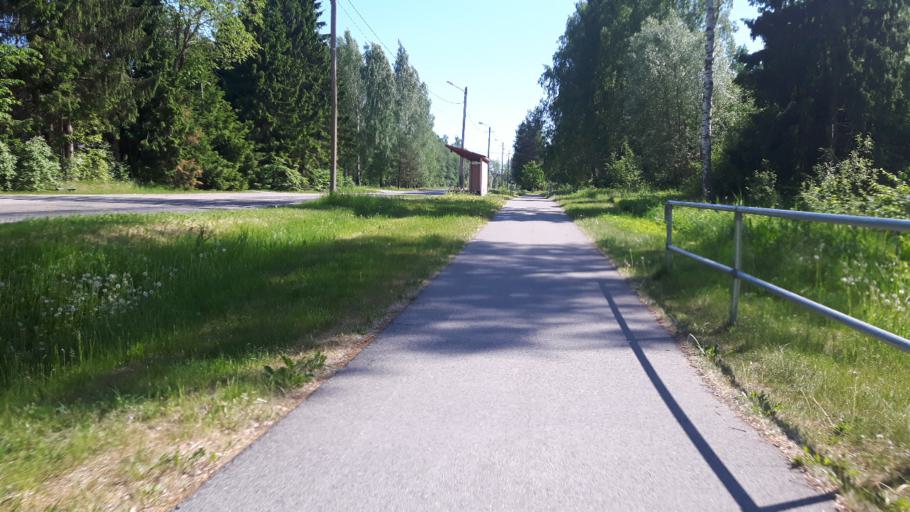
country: EE
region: Paernumaa
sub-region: Paikuse vald
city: Paikuse
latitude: 58.3929
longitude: 24.6410
